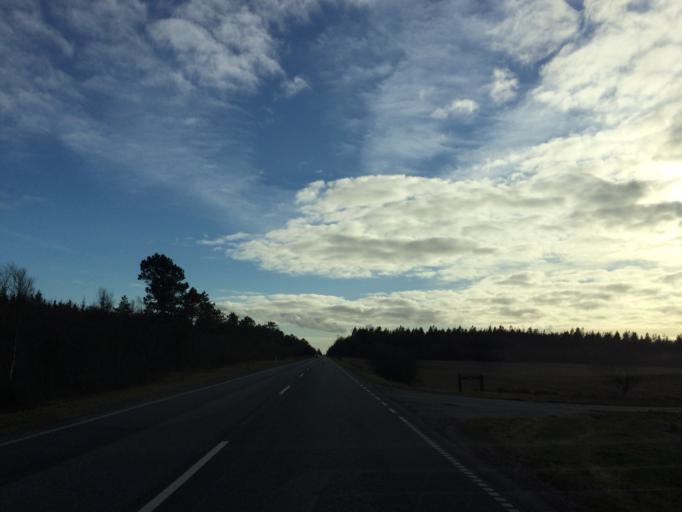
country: DK
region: Central Jutland
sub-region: Lemvig Kommune
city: Lemvig
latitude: 56.4724
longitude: 8.2976
